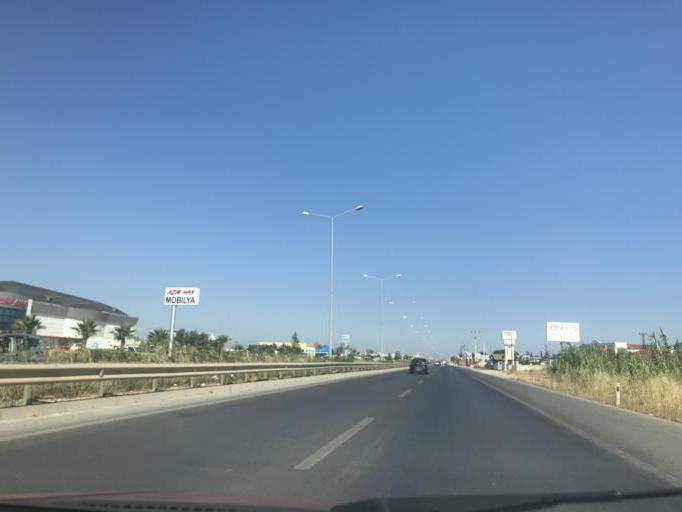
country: TR
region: Antalya
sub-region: Manavgat
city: Side
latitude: 36.8102
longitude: 31.3783
